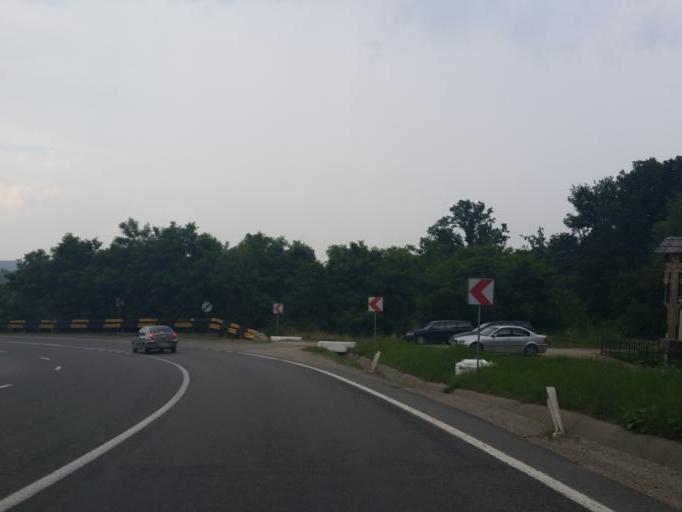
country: RO
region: Salaj
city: Zalau
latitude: 47.1600
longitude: 23.0894
